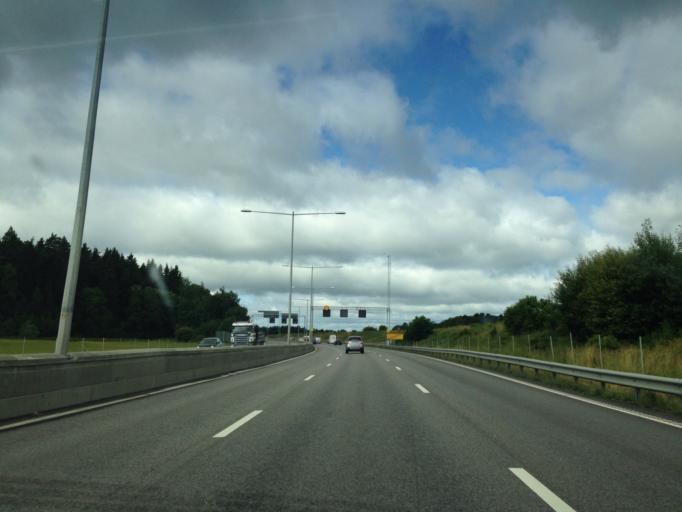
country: SE
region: Stockholm
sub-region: Botkyrka Kommun
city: Eriksberg
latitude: 59.2381
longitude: 17.8206
